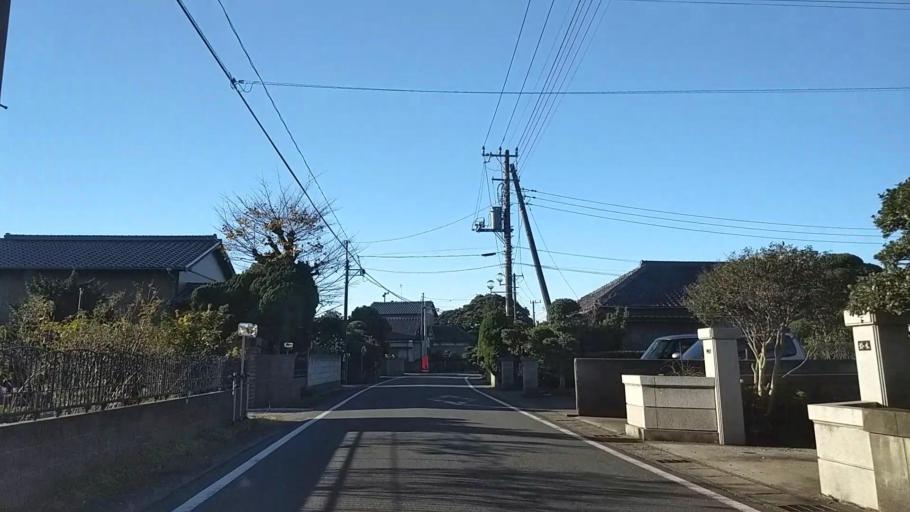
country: JP
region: Chiba
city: Kisarazu
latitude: 35.4285
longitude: 139.9221
